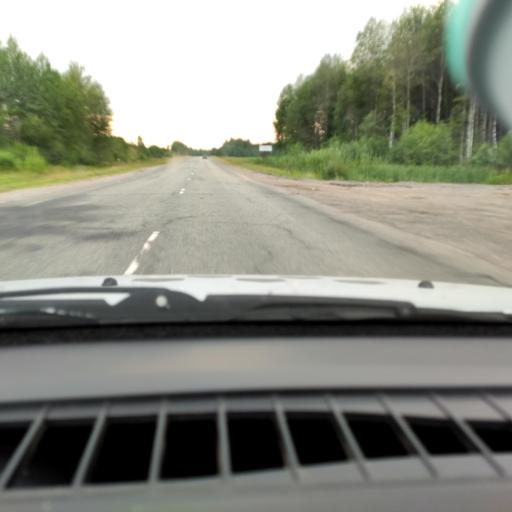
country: RU
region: Udmurtiya
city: Debesy
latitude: 57.6056
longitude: 53.4775
